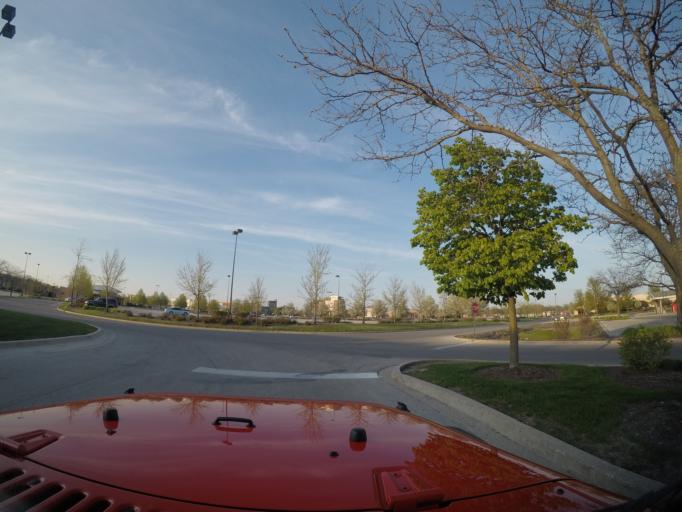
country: US
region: Illinois
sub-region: Cook County
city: Prospect Heights
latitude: 42.0816
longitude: -87.9359
